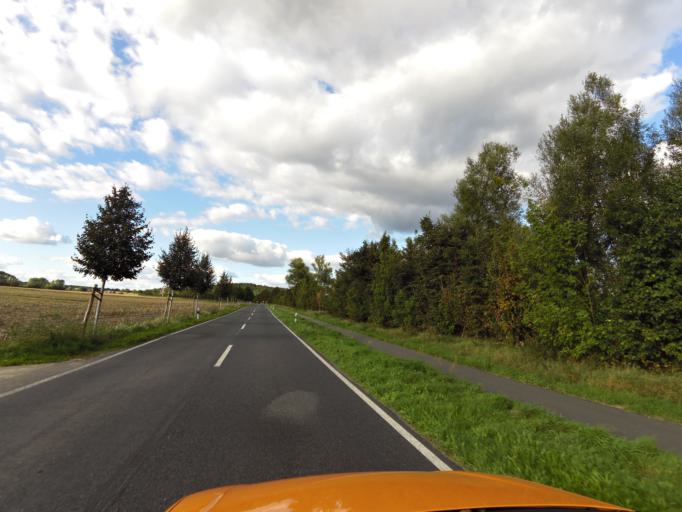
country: DE
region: Brandenburg
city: Trebbin
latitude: 52.1768
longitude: 13.1762
